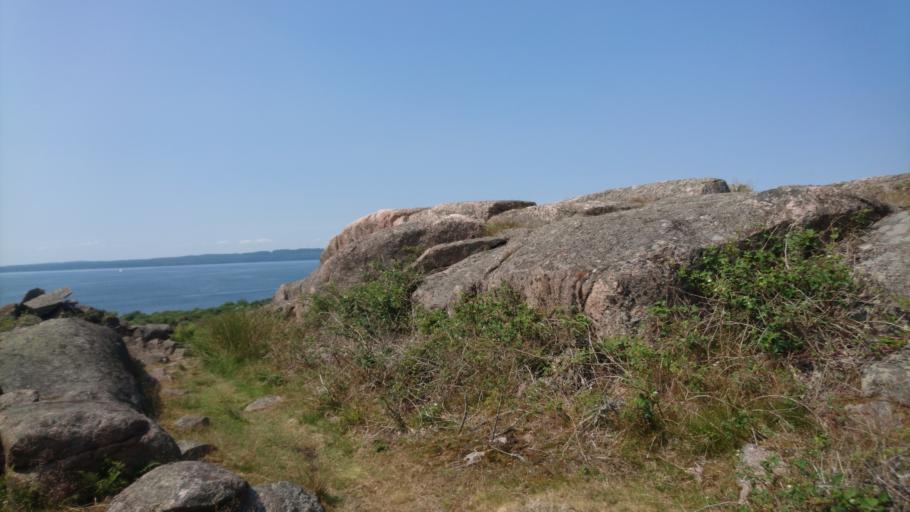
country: SE
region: Blekinge
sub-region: Karlshamns Kommun
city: Karlshamn
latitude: 56.0153
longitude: 14.8407
